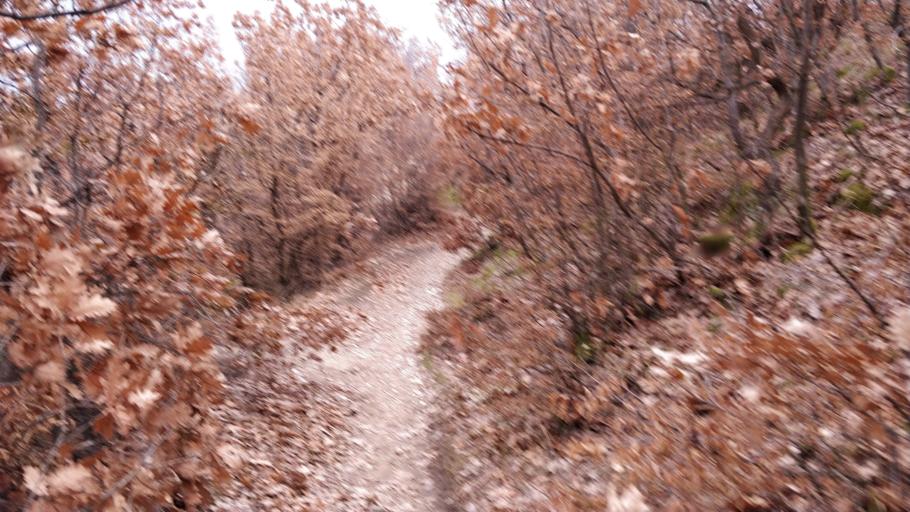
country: BG
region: Kyustendil
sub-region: Obshtina Rila
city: Rila
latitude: 42.0937
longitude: 23.1162
